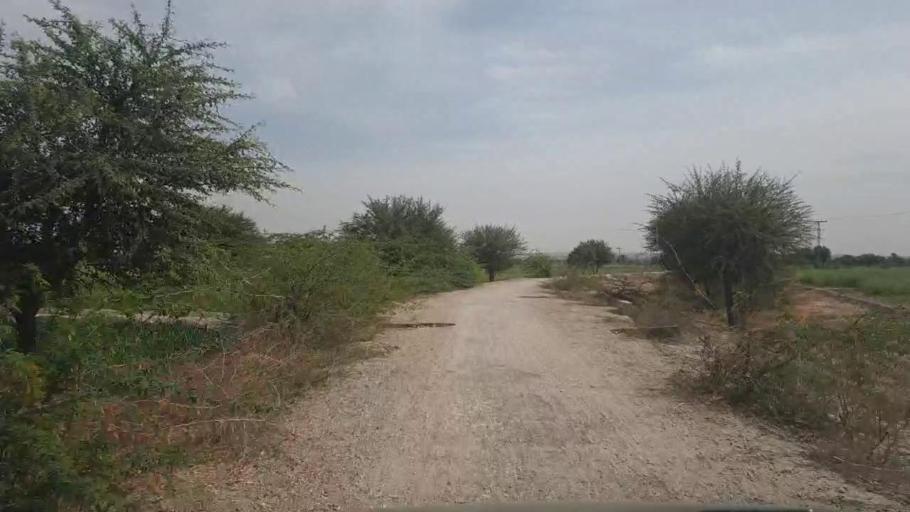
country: PK
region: Sindh
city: Kunri
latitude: 25.1946
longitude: 69.6913
